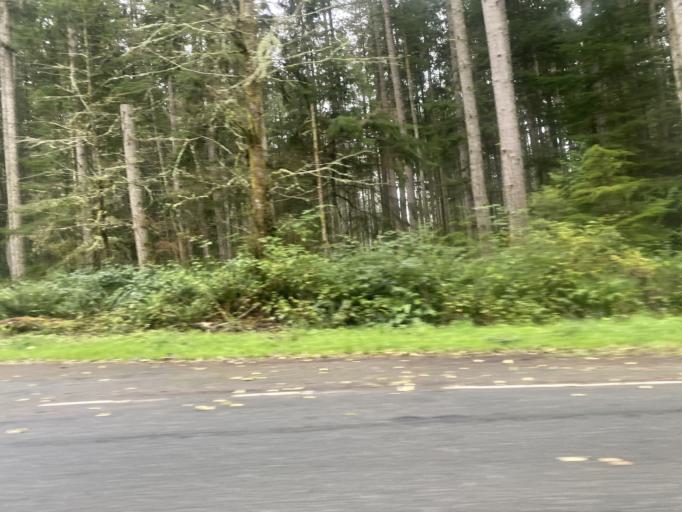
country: US
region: Washington
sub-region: Island County
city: Freeland
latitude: 48.0658
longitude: -122.4852
